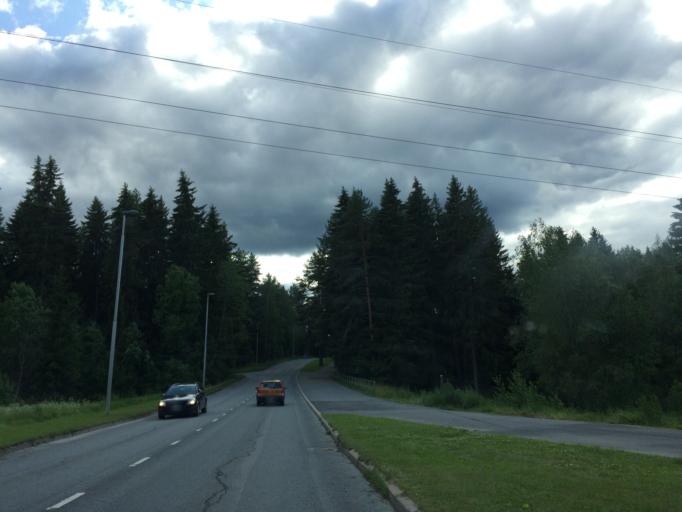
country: FI
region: Haeme
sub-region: Haemeenlinna
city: Haemeenlinna
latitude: 60.9767
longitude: 24.3993
